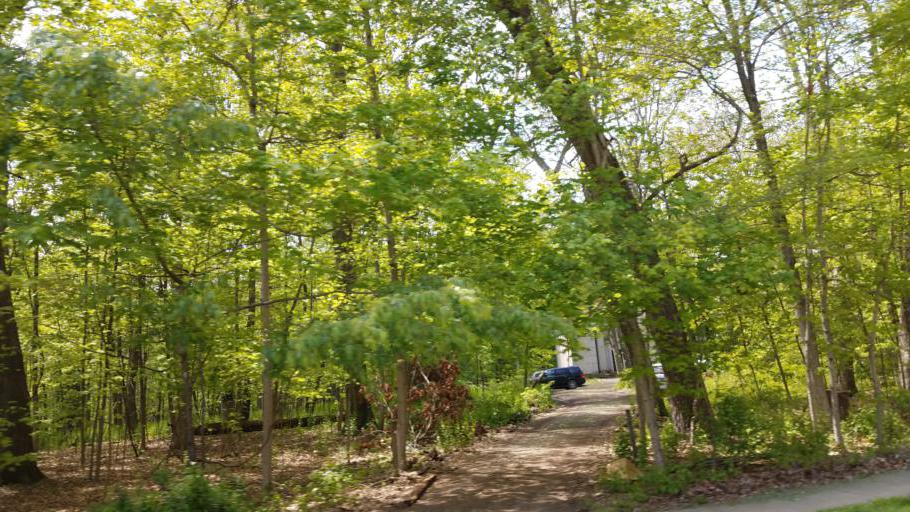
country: US
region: Ohio
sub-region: Knox County
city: Gambier
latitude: 40.3820
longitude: -82.3978
